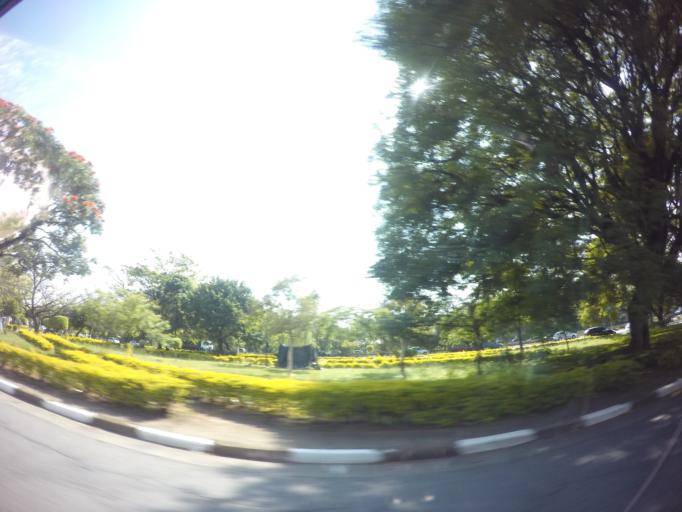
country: BR
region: Sao Paulo
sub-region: Sao Paulo
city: Sao Paulo
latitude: -23.5133
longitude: -46.6218
